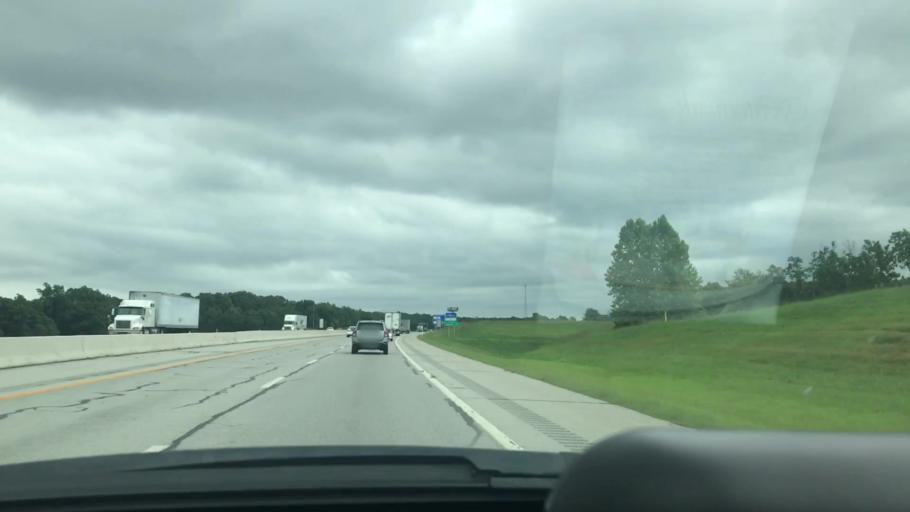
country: US
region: Kansas
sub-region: Cherokee County
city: Galena
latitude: 36.9946
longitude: -94.6207
